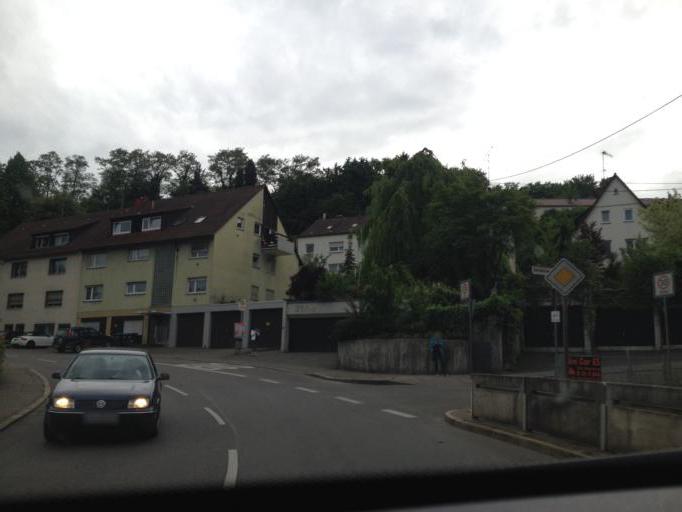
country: DE
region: Baden-Wuerttemberg
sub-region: Regierungsbezirk Stuttgart
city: Esslingen
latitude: 48.7439
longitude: 9.3285
